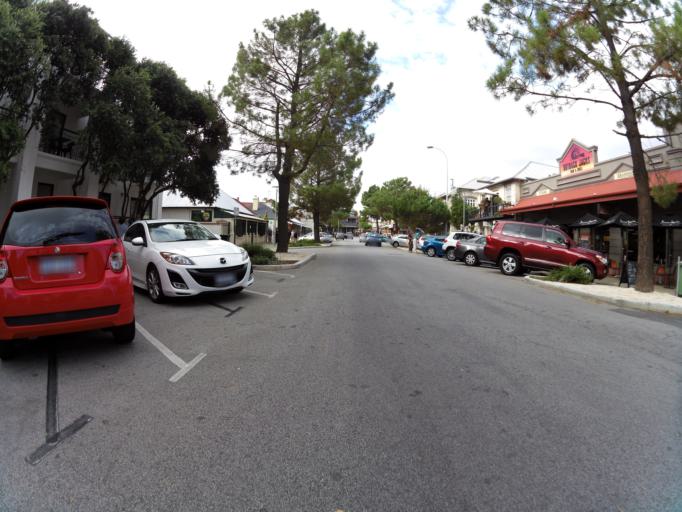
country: AU
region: Western Australia
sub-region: Fremantle
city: South Fremantle
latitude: -32.0570
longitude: 115.7474
